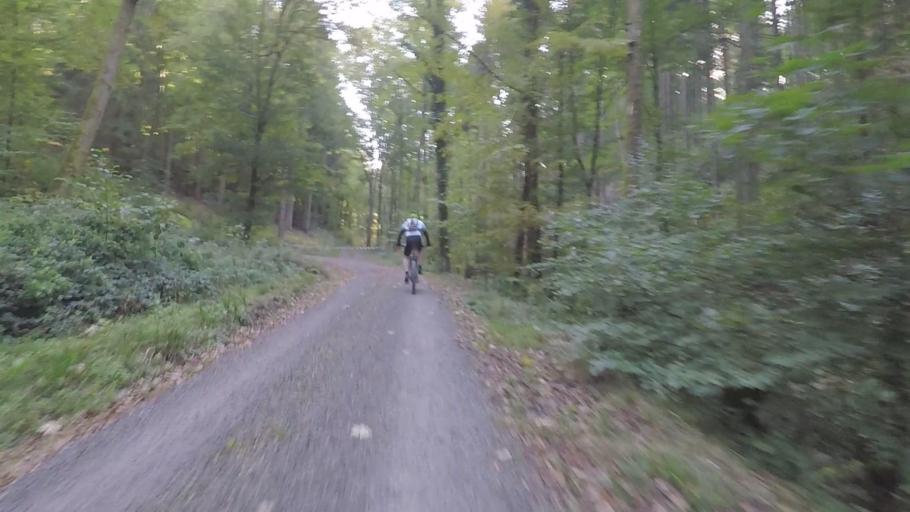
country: DE
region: Baden-Wuerttemberg
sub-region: Regierungsbezirk Stuttgart
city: Spiegelberg
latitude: 49.0439
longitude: 9.4516
